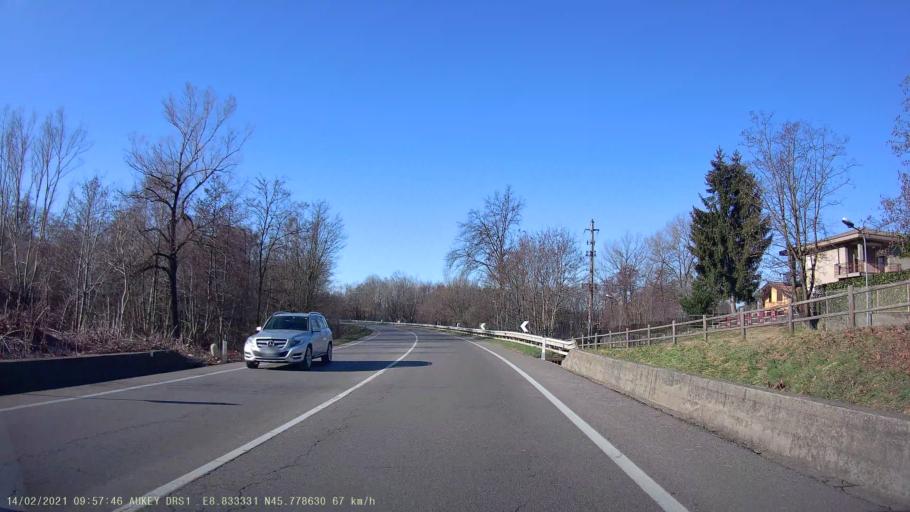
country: IT
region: Lombardy
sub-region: Provincia di Varese
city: Gazzada Schianno
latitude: 45.7785
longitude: 8.8326
